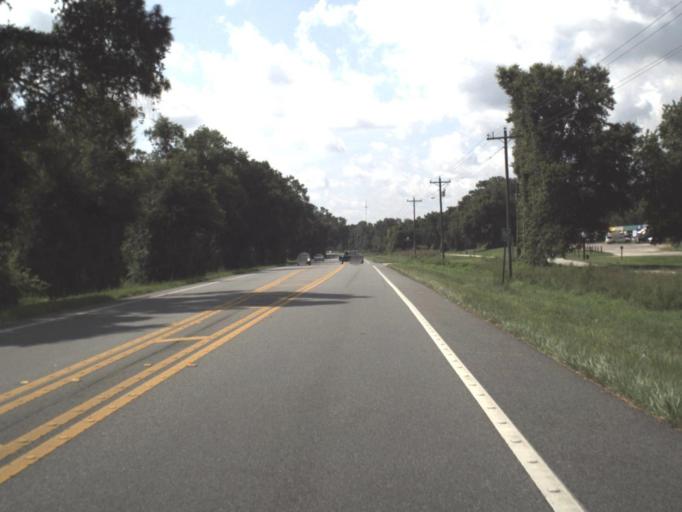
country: US
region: Florida
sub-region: Citrus County
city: Inverness Highlands North
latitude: 28.8706
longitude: -82.3608
